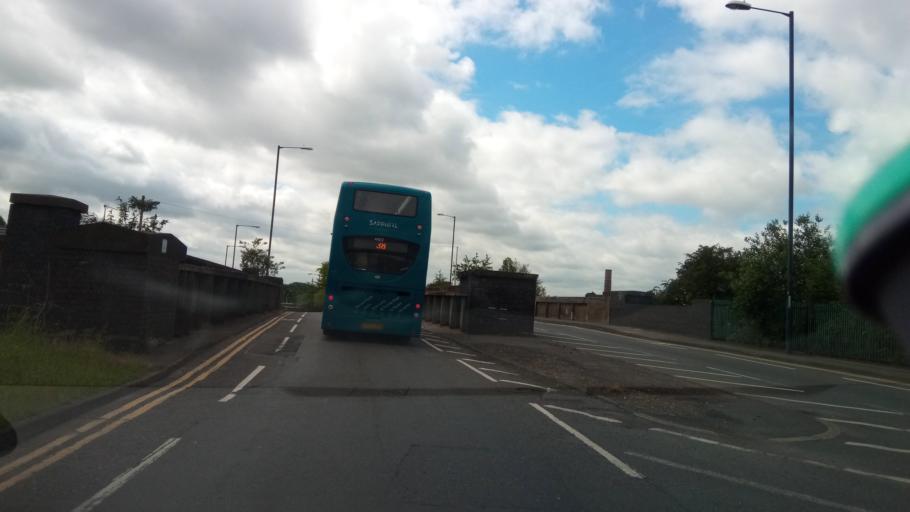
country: GB
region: England
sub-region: Derby
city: Derby
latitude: 52.8936
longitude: -1.4796
